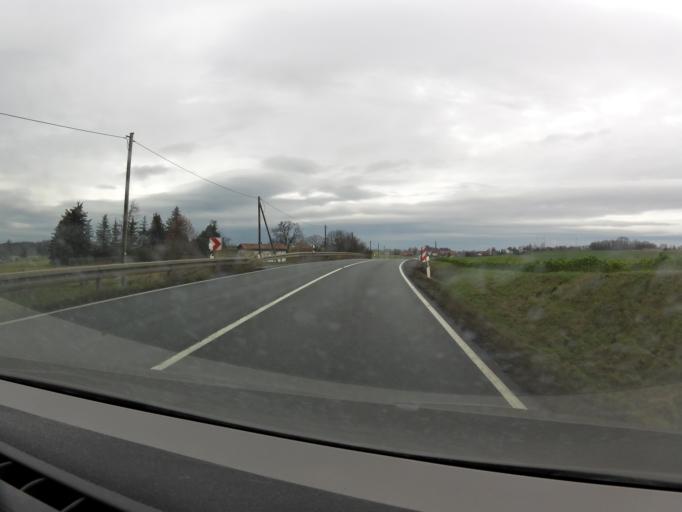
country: DE
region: Saxony-Anhalt
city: Hettstedt
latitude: 51.6850
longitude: 11.4556
